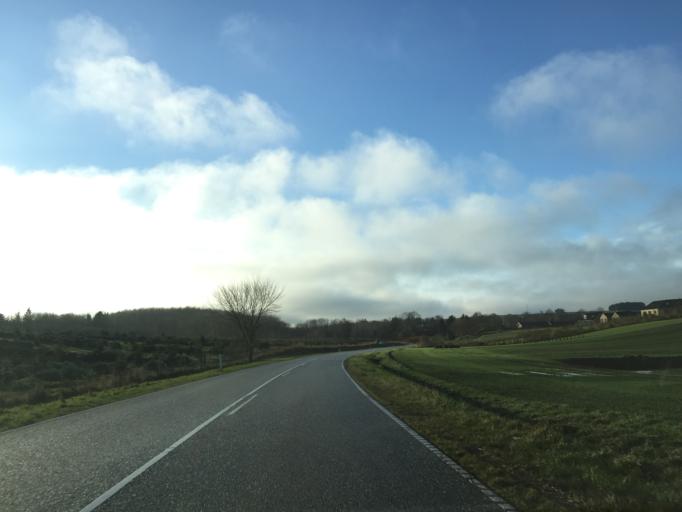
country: DK
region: Central Jutland
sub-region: Favrskov Kommune
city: Hammel
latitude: 56.1754
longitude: 9.8261
